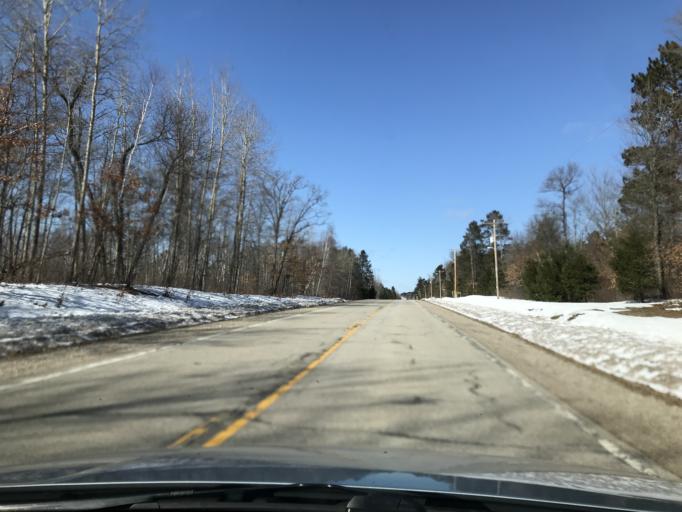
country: US
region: Wisconsin
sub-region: Marinette County
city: Niagara
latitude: 45.3560
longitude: -88.1010
